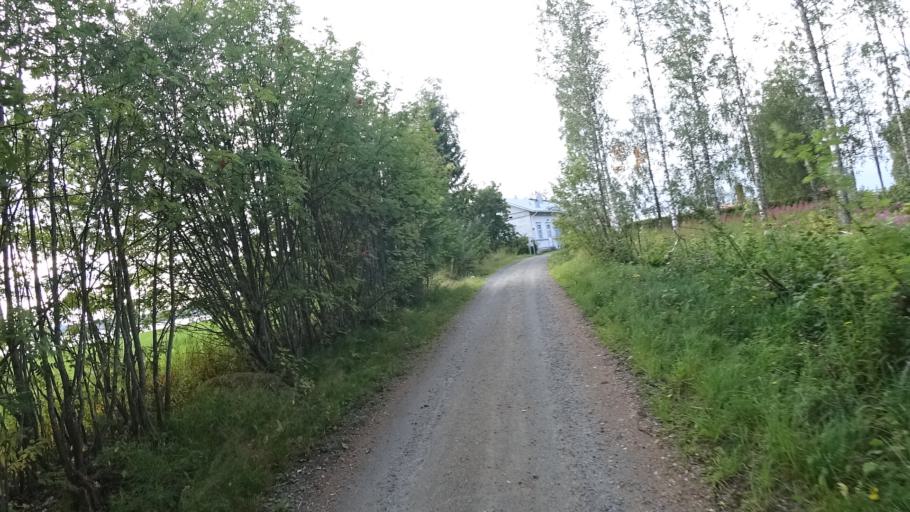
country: FI
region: North Karelia
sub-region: Joensuu
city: Ilomantsi
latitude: 62.6715
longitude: 30.9195
